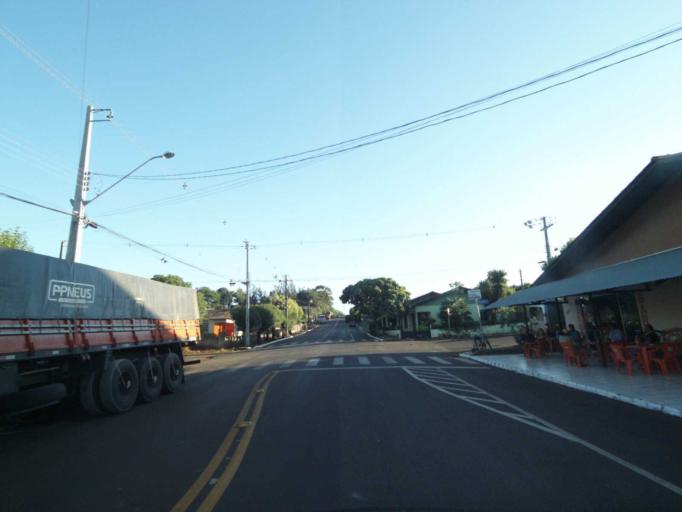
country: BR
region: Parana
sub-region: Coronel Vivida
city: Coronel Vivida
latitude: -25.9727
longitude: -52.8153
